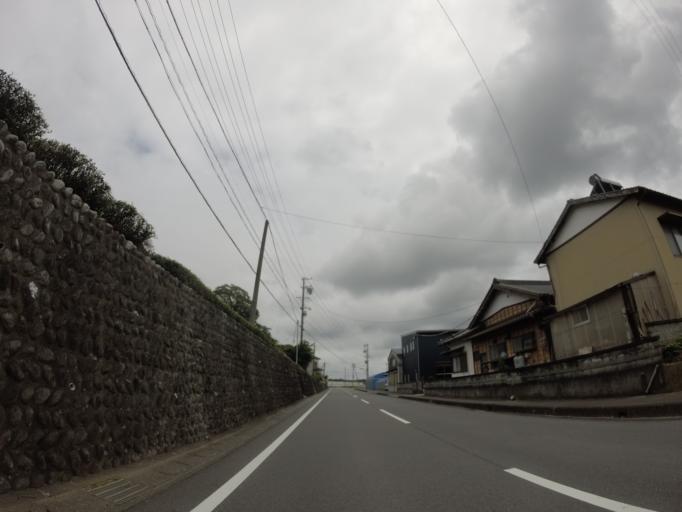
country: JP
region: Shizuoka
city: Shimada
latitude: 34.7641
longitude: 138.1952
